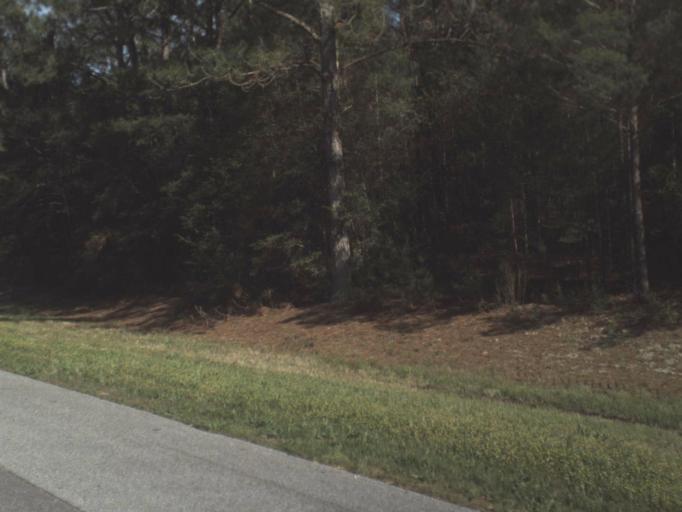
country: US
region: Florida
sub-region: Okaloosa County
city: Crestview
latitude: 30.7189
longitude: -86.4296
